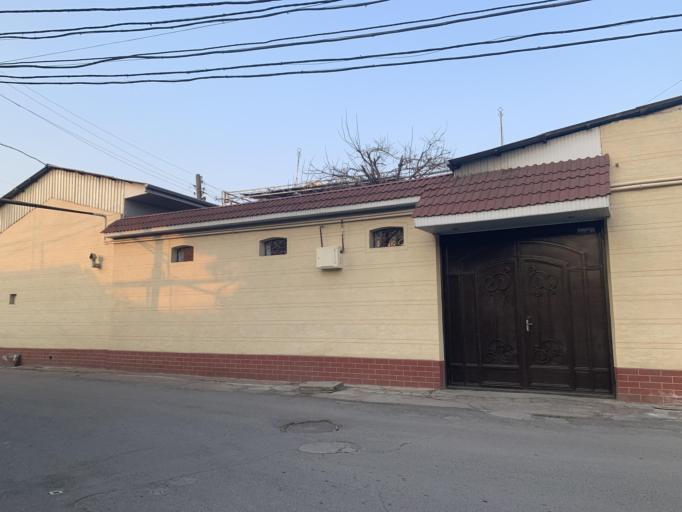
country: UZ
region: Fergana
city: Qo`qon
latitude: 40.5318
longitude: 70.9312
